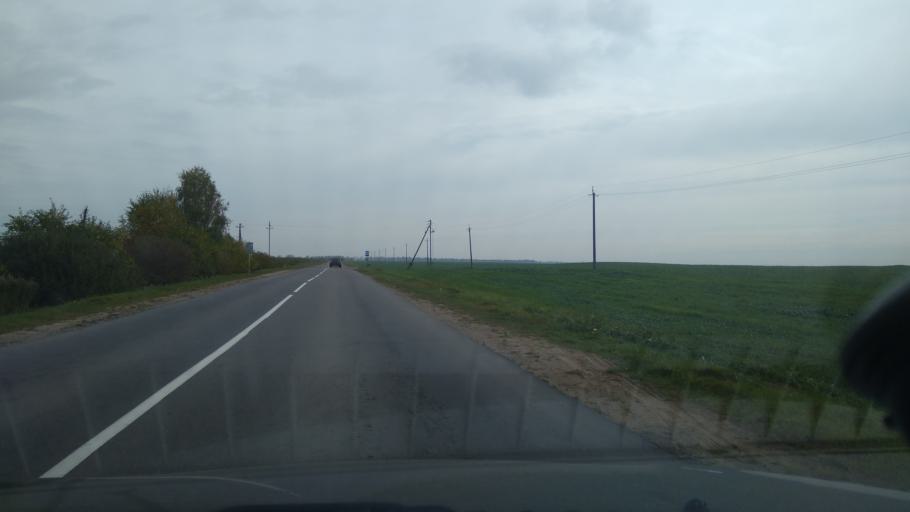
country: BY
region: Minsk
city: Rudzyensk
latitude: 53.6103
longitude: 27.8035
